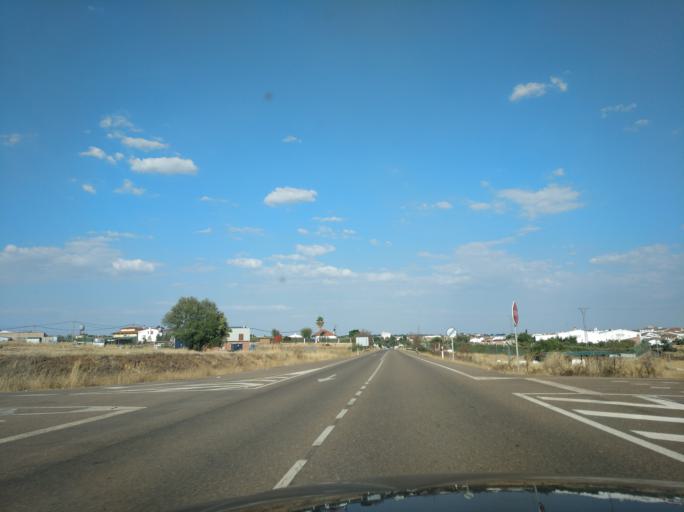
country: ES
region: Extremadura
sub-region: Provincia de Badajoz
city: Villanueva del Fresno
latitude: 38.3771
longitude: -7.1781
